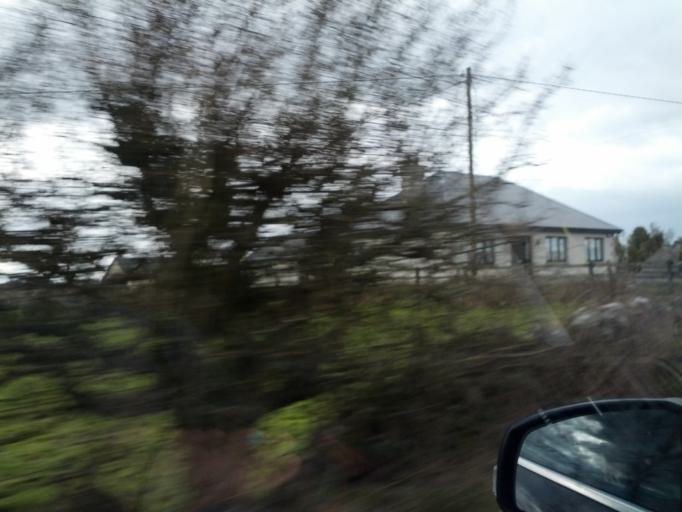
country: IE
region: Connaught
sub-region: County Galway
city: Athenry
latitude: 53.4623
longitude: -8.6315
